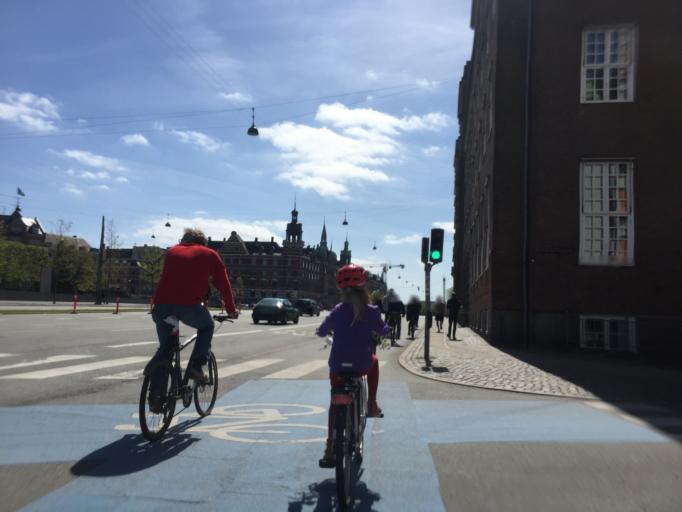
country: DK
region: Capital Region
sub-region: Kobenhavn
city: Copenhagen
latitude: 55.6794
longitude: 12.5635
